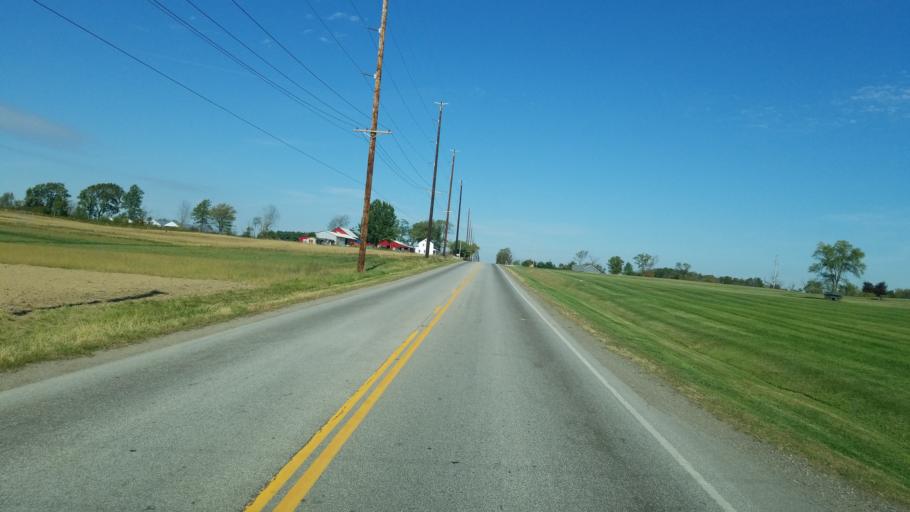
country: US
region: Ohio
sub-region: Wayne County
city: West Salem
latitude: 40.9939
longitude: -82.1110
